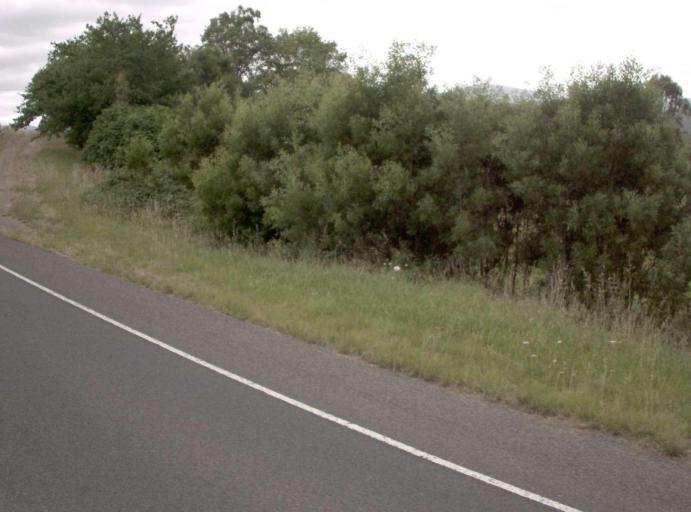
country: AU
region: Victoria
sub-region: Yarra Ranges
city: Yarra Glen
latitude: -37.6165
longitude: 145.4098
